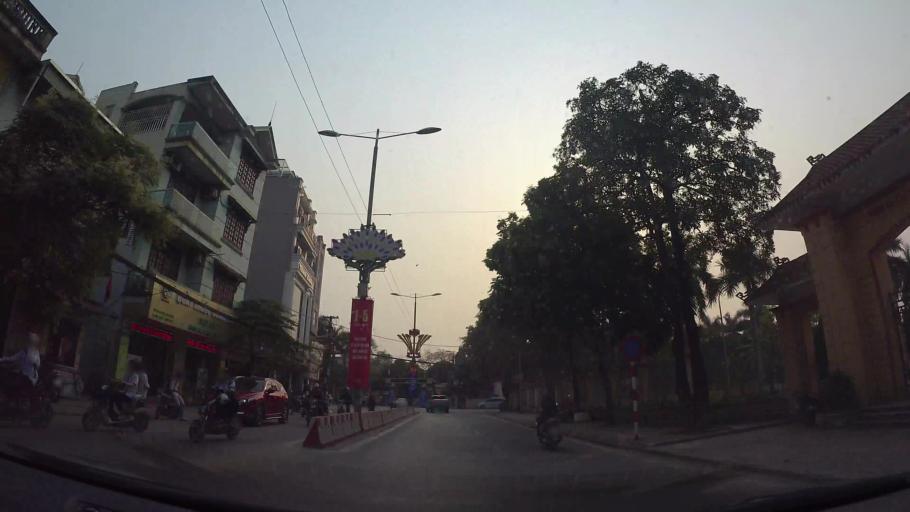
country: VN
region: Ha Noi
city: Thuong Tin
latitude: 20.8691
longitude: 105.8627
